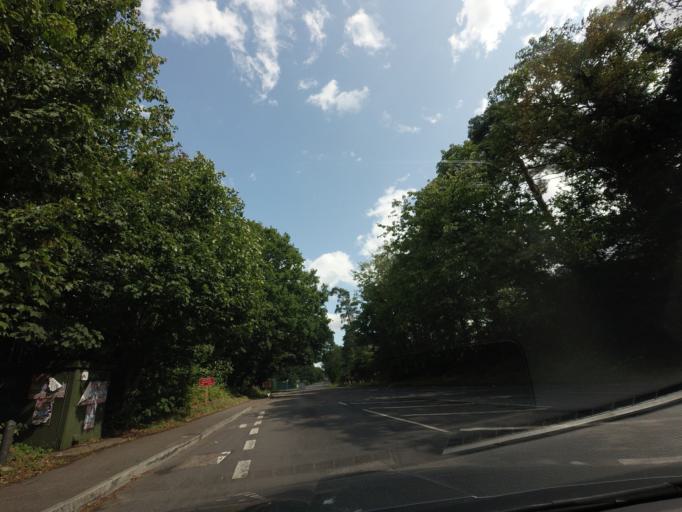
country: GB
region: England
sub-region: Kent
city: Boxley
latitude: 51.2674
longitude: 0.5914
